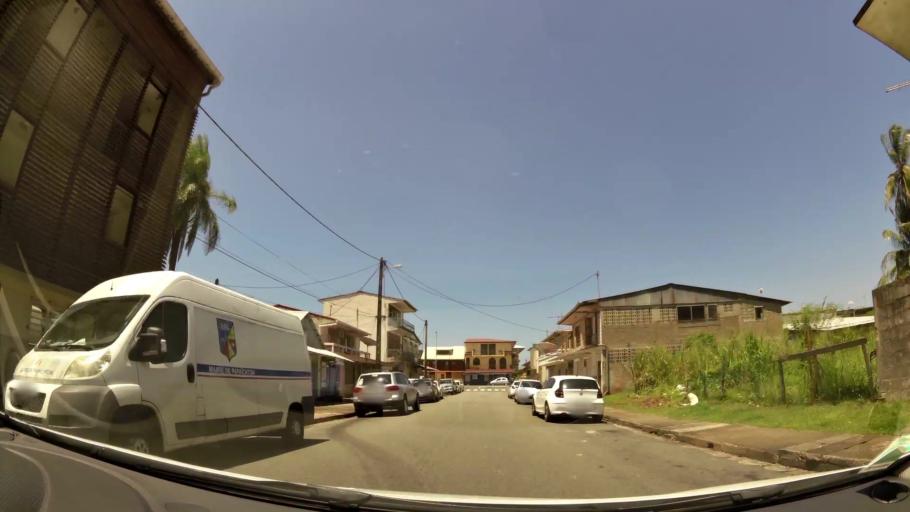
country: GF
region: Guyane
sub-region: Guyane
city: Cayenne
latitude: 4.9353
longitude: -52.3282
